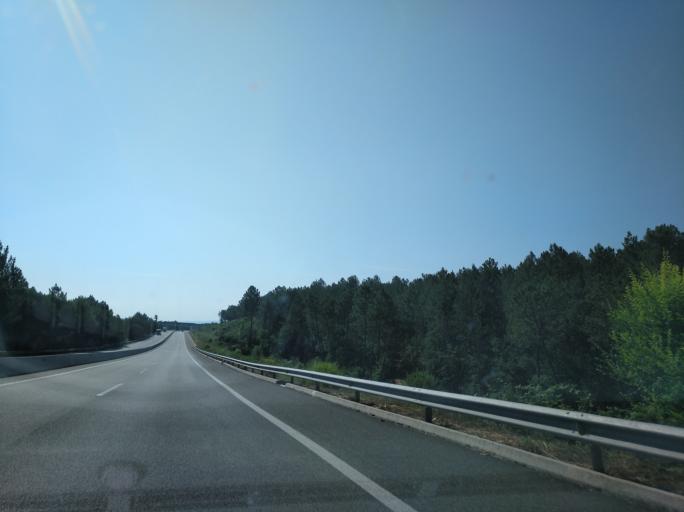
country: ES
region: Catalonia
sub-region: Provincia de Girona
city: Brunyola
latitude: 41.8904
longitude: 2.6675
